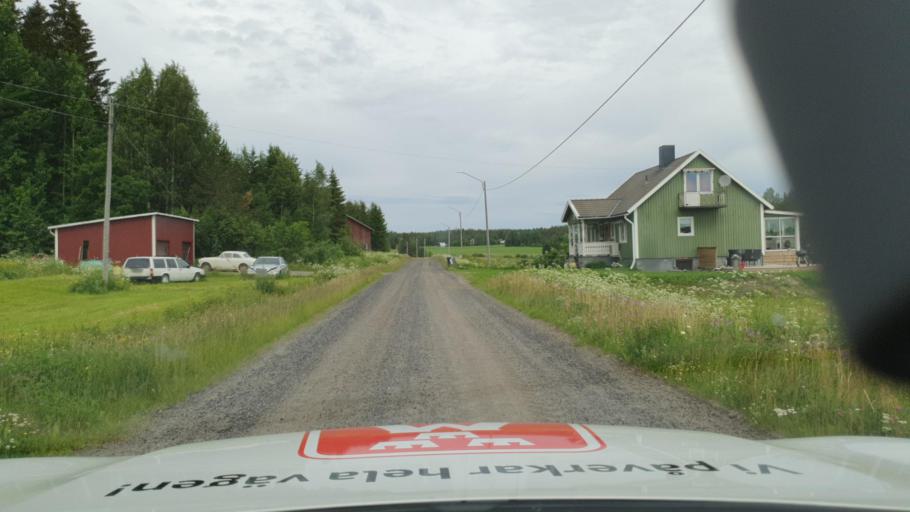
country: SE
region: Vaesterbotten
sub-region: Robertsfors Kommun
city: Robertsfors
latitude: 64.1837
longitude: 20.7324
